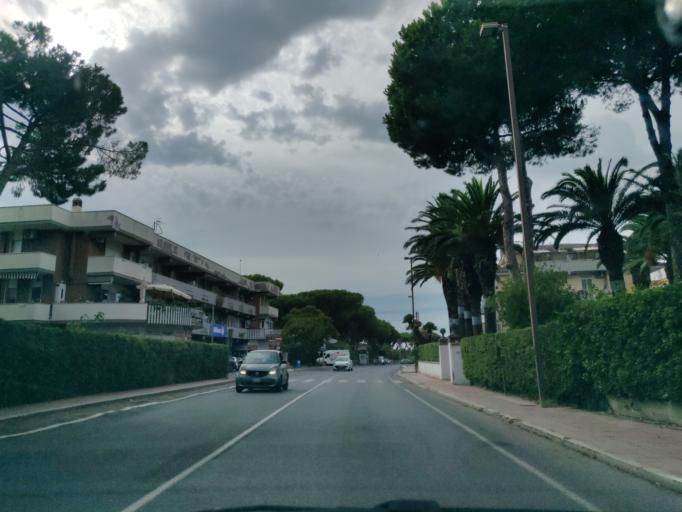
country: IT
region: Latium
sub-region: Citta metropolitana di Roma Capitale
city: Santa Marinella
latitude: 42.0327
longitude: 11.8389
